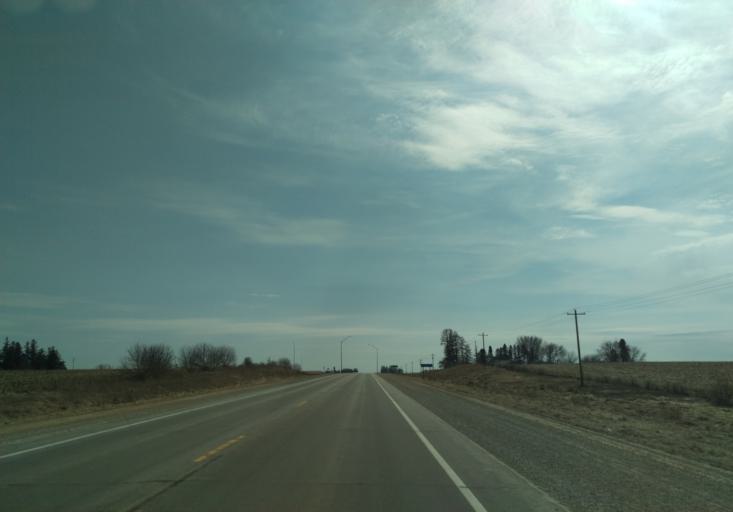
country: US
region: Iowa
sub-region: Winneshiek County
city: Decorah
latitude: 43.4459
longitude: -91.8623
